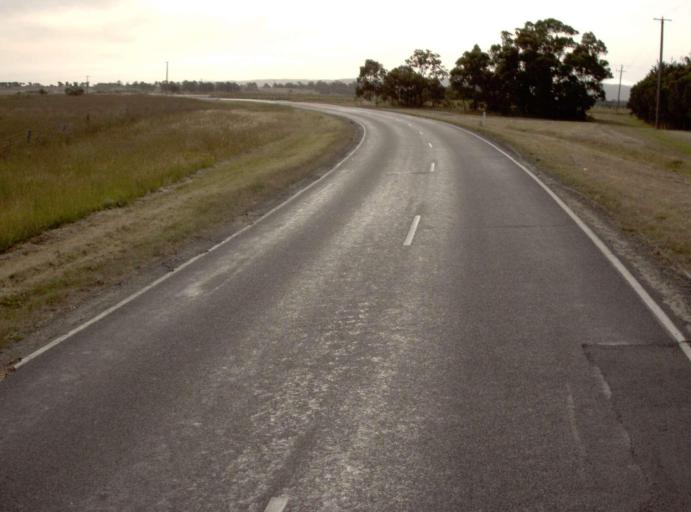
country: AU
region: Victoria
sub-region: Wellington
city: Heyfield
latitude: -38.0186
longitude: 146.7387
